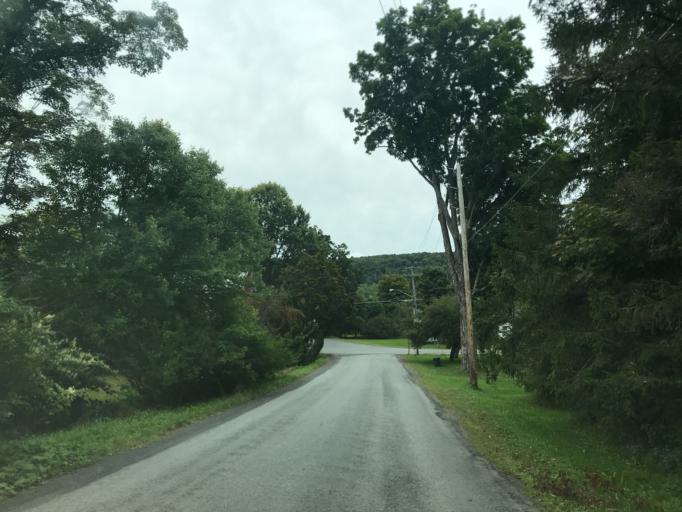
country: US
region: New York
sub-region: Otsego County
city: Worcester
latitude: 42.5458
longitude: -74.6650
